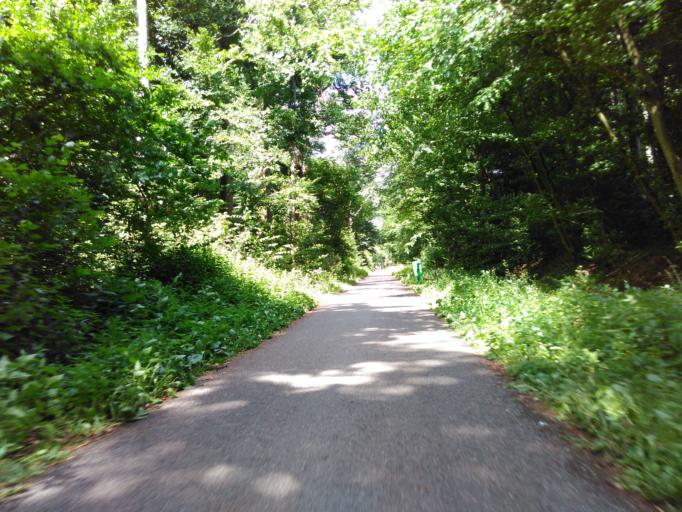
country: LU
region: Luxembourg
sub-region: Canton de Capellen
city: Clemency
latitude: 49.6222
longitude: 5.8795
